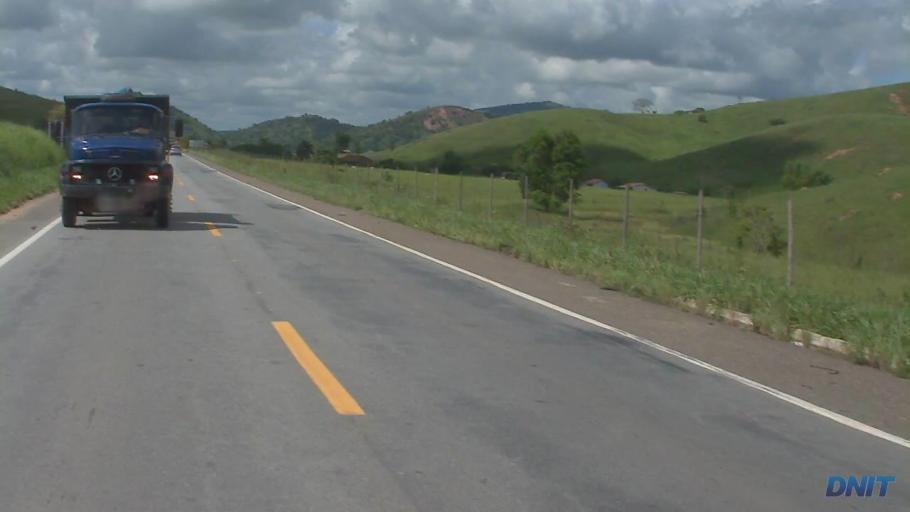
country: BR
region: Minas Gerais
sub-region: Belo Oriente
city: Belo Oriente
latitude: -19.1326
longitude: -42.2133
